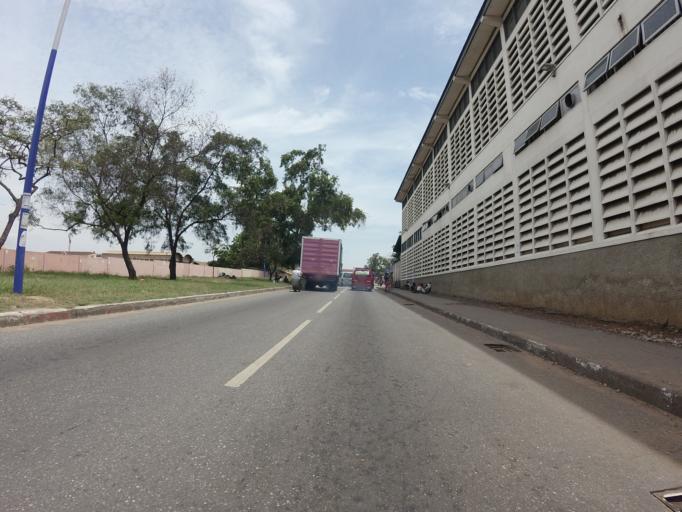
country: GH
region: Greater Accra
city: Accra
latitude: 5.5546
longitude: -0.2160
